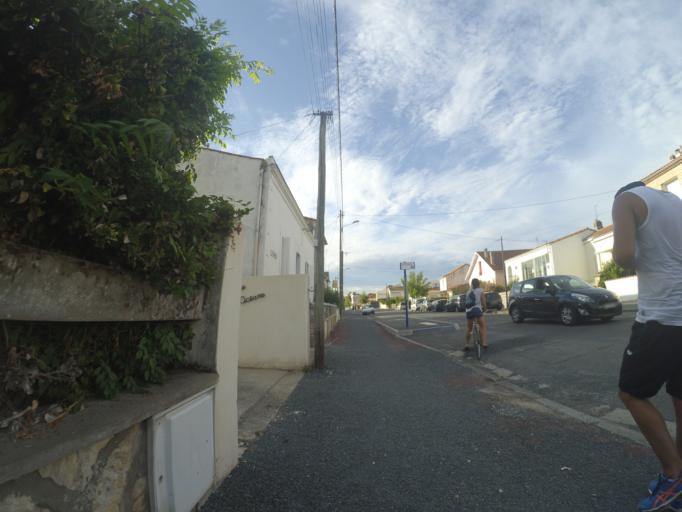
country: FR
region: Poitou-Charentes
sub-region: Departement de la Charente-Maritime
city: Saint-Georges-de-Didonne
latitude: 45.6026
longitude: -1.0027
